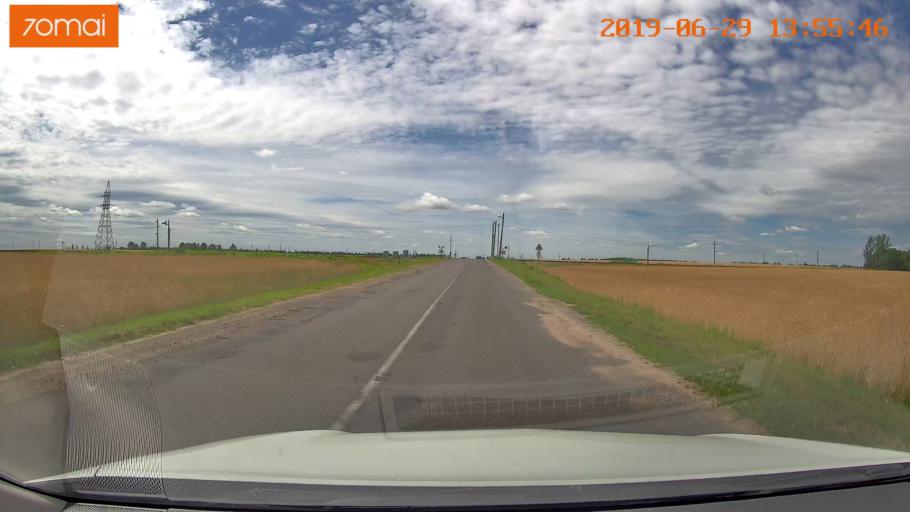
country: BY
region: Minsk
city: Slutsk
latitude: 52.9846
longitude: 27.5134
